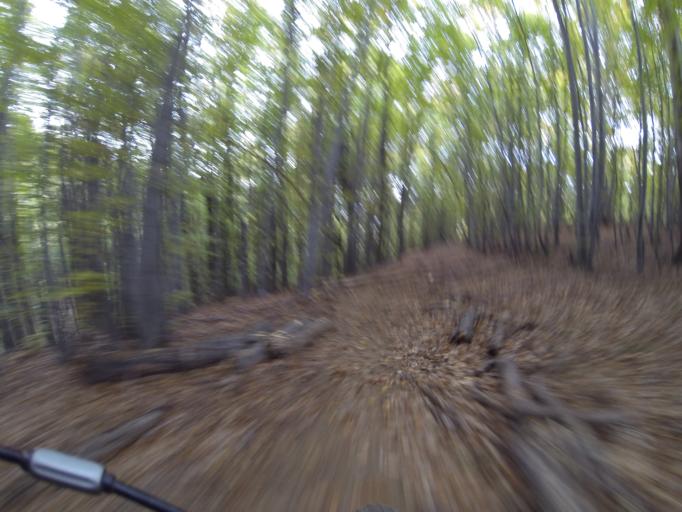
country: RO
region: Gorj
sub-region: Comuna Tismana
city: Sohodol
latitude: 45.0902
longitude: 22.8857
